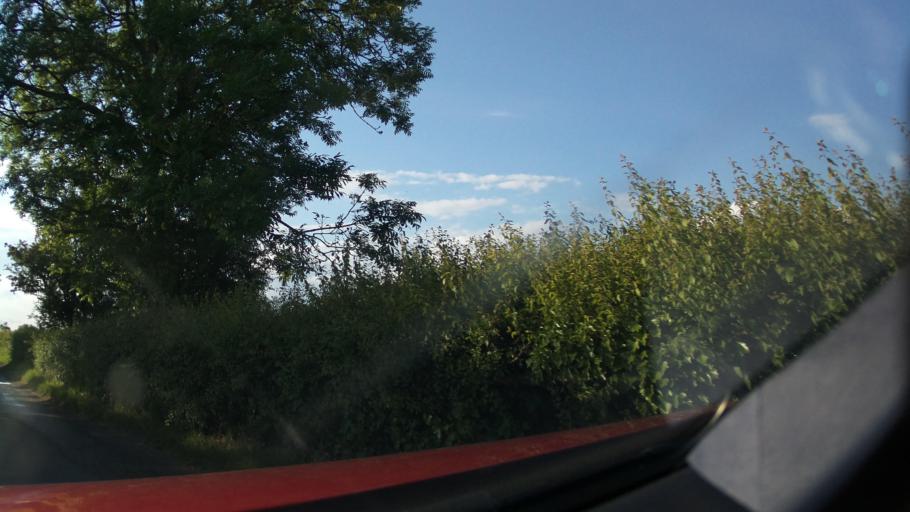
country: GB
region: England
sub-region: Lincolnshire
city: Navenby
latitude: 53.1165
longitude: -0.6222
